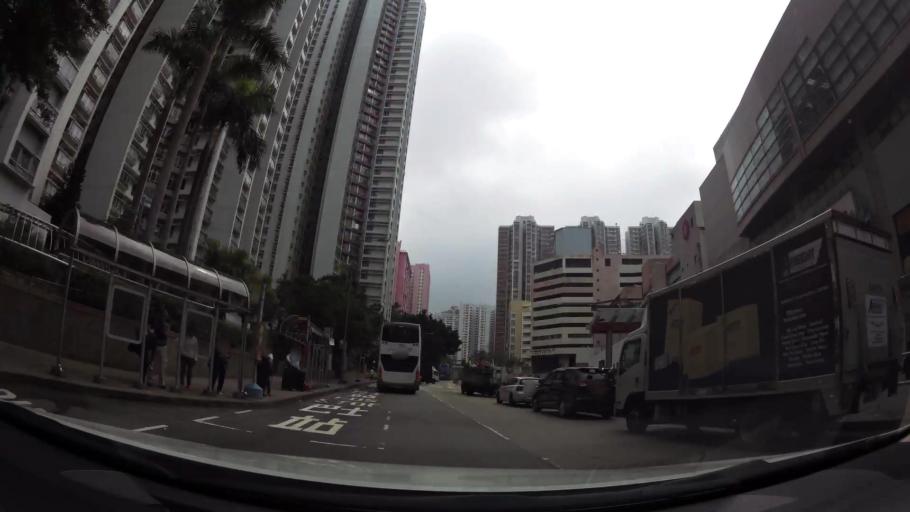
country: HK
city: Yung Shue Wan
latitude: 22.2444
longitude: 114.1469
